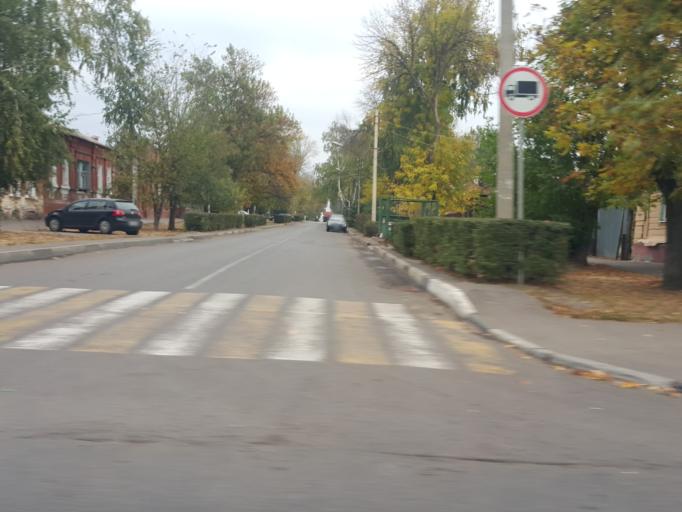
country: RU
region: Tambov
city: Tambov
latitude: 52.7155
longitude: 41.4552
